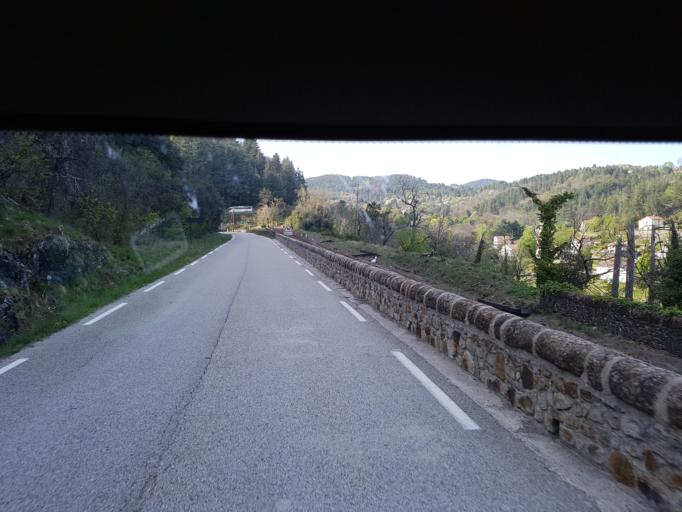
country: FR
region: Languedoc-Roussillon
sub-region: Departement du Gard
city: Branoux-les-Taillades
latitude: 44.3400
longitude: 3.9522
